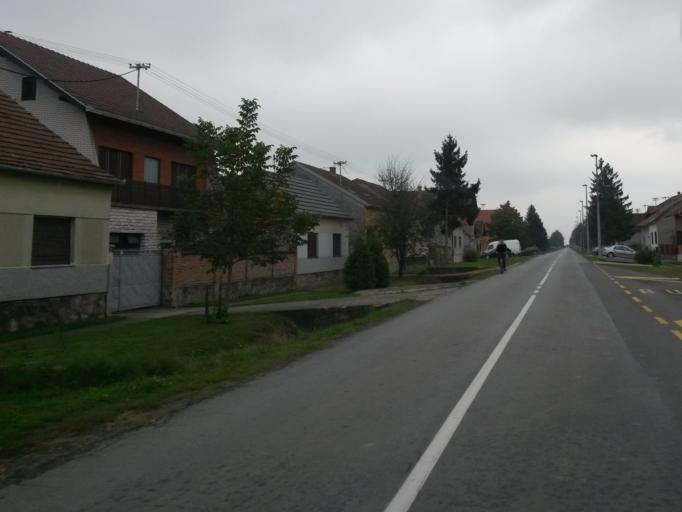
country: HR
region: Osjecko-Baranjska
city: Brijest
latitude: 45.5241
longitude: 18.6272
